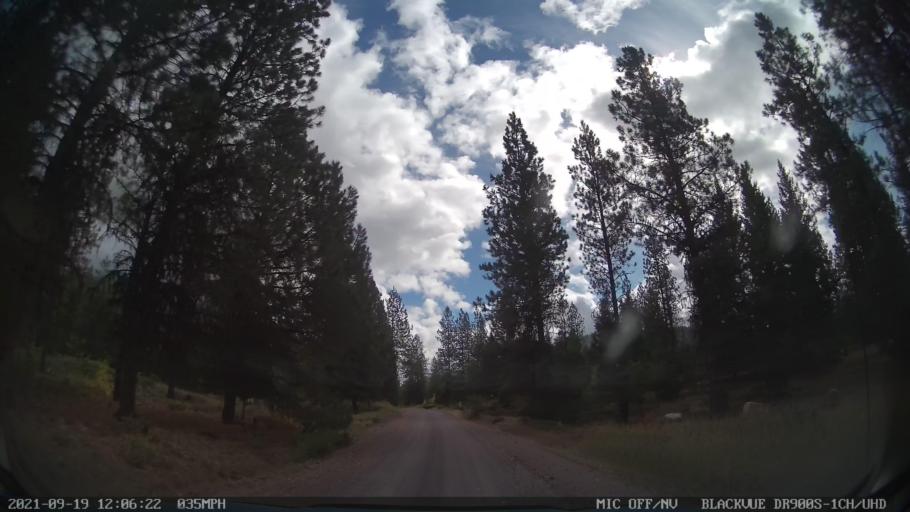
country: US
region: Montana
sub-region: Missoula County
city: Seeley Lake
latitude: 47.1854
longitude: -113.4199
